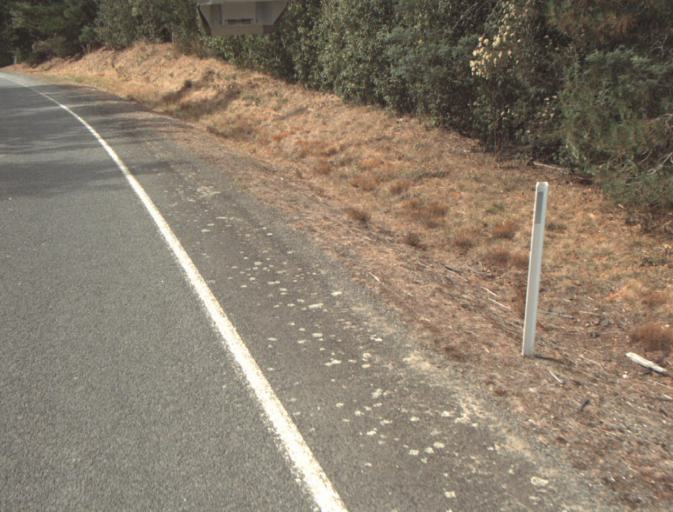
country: AU
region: Tasmania
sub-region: Launceston
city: Mayfield
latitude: -41.2707
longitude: 147.2146
